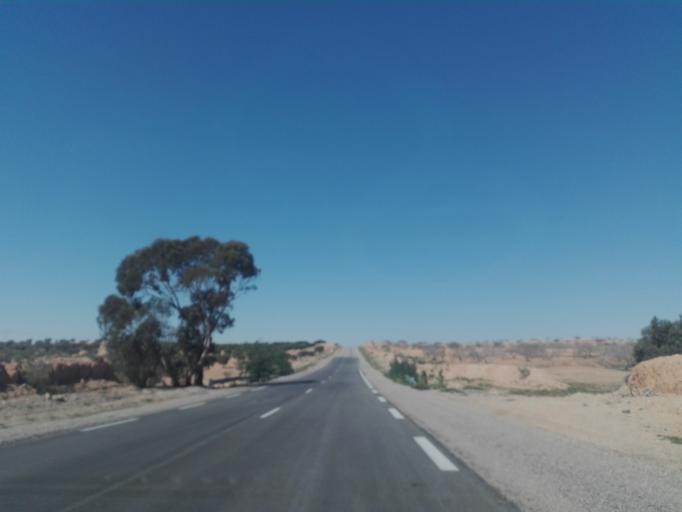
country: TN
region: Safaqis
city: Bi'r `Ali Bin Khalifah
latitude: 34.7580
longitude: 10.2844
